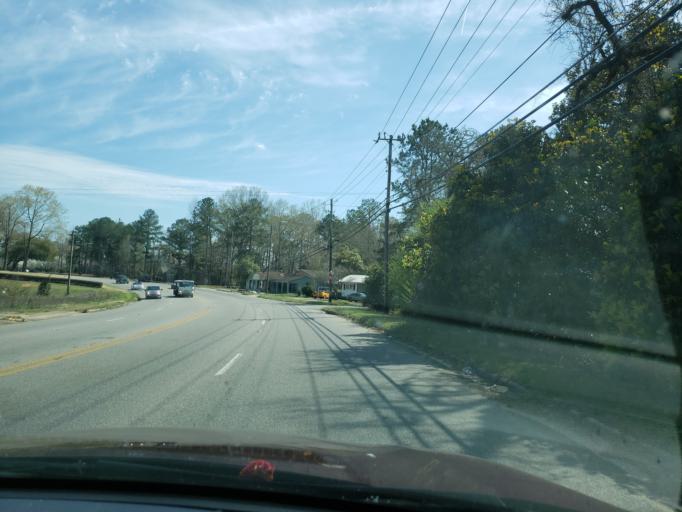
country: US
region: Alabama
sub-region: Elmore County
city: Tallassee
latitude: 32.5451
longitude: -85.9108
